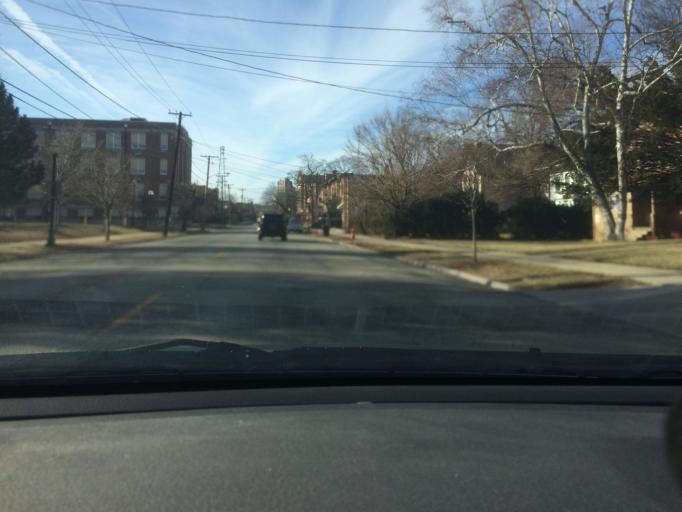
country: US
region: Illinois
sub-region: Kane County
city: Elgin
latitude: 42.0373
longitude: -88.2763
